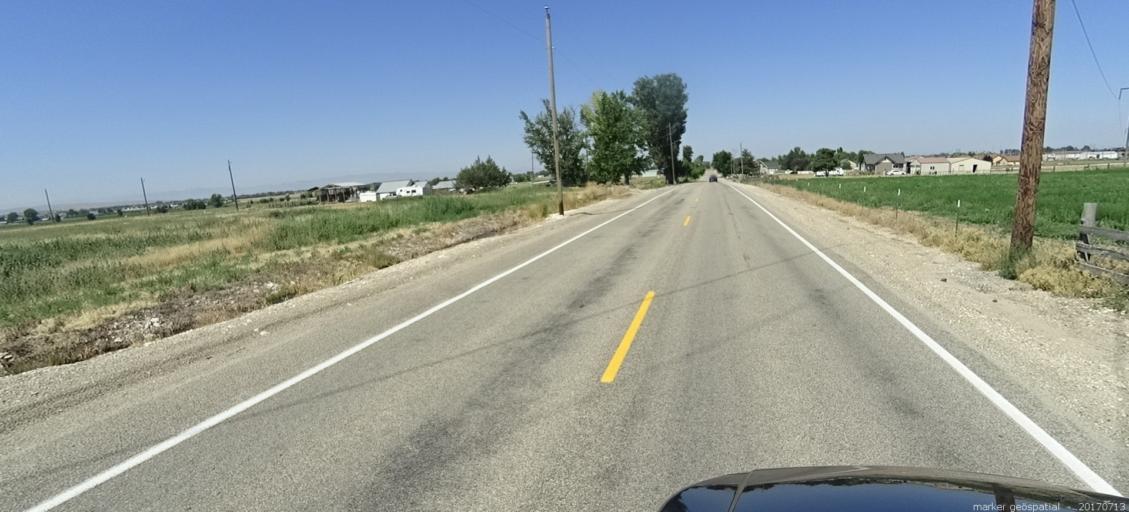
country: US
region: Idaho
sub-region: Ada County
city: Kuna
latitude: 43.5319
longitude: -116.3827
